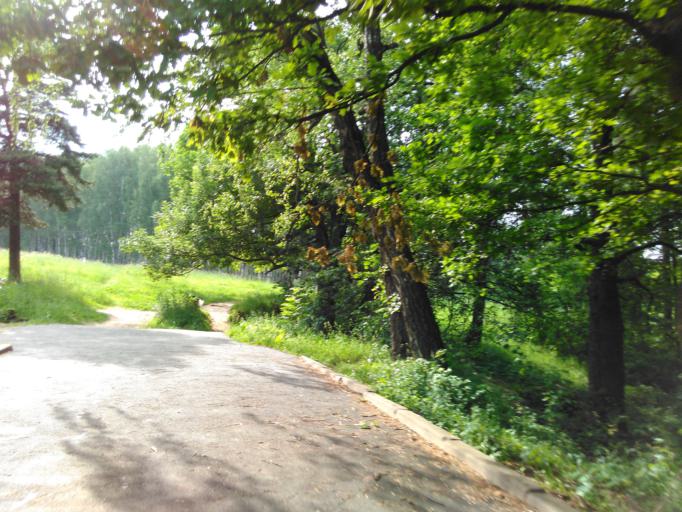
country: RU
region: Moscow
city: Yasenevo
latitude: 55.6239
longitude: 37.5336
